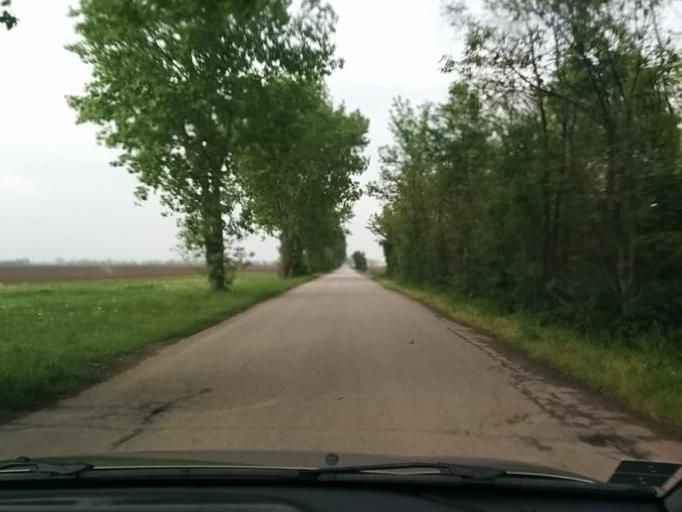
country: SK
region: Trnavsky
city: Sladkovicovo
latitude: 48.2359
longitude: 17.5822
